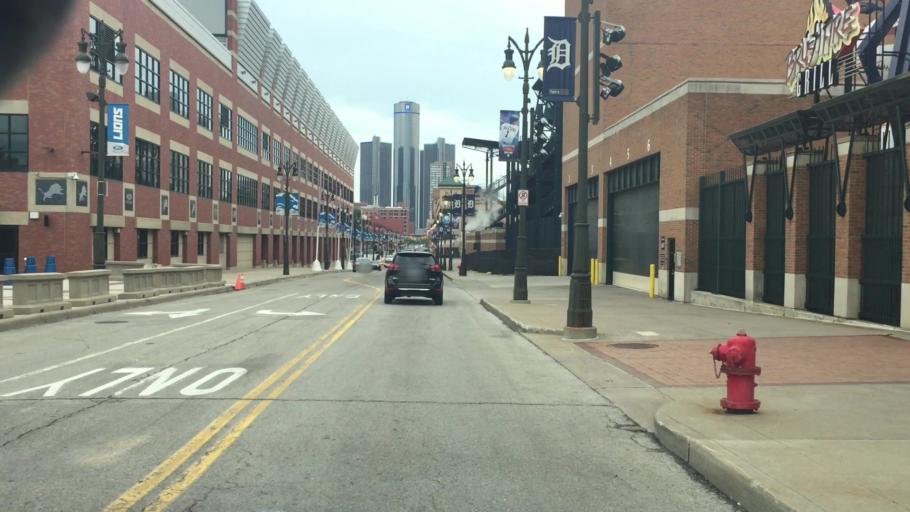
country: US
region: Michigan
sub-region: Wayne County
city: Detroit
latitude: 42.3405
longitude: -83.0478
